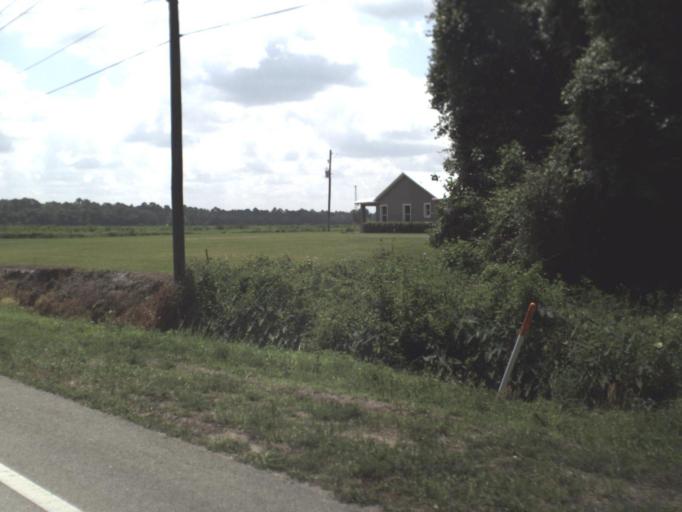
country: US
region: Florida
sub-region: Putnam County
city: East Palatka
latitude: 29.7256
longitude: -81.4722
